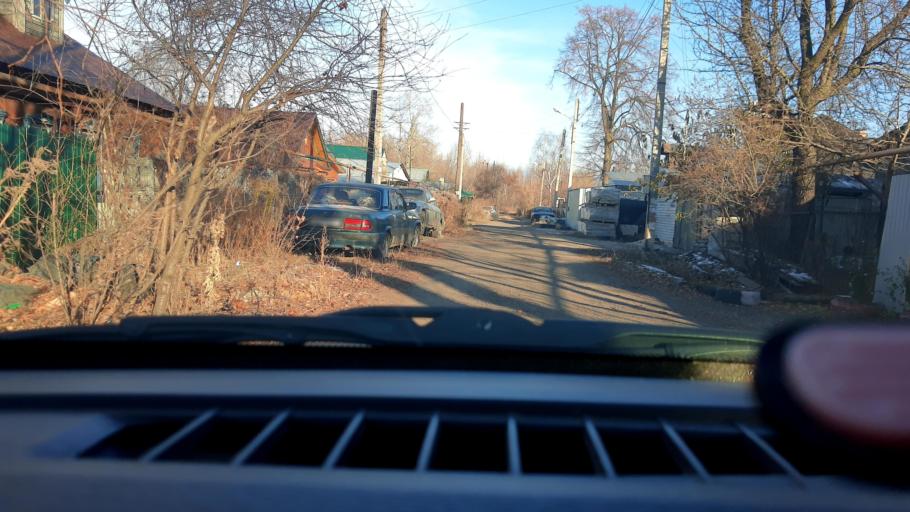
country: RU
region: Nizjnij Novgorod
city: Nizhniy Novgorod
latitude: 56.2986
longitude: 43.9179
